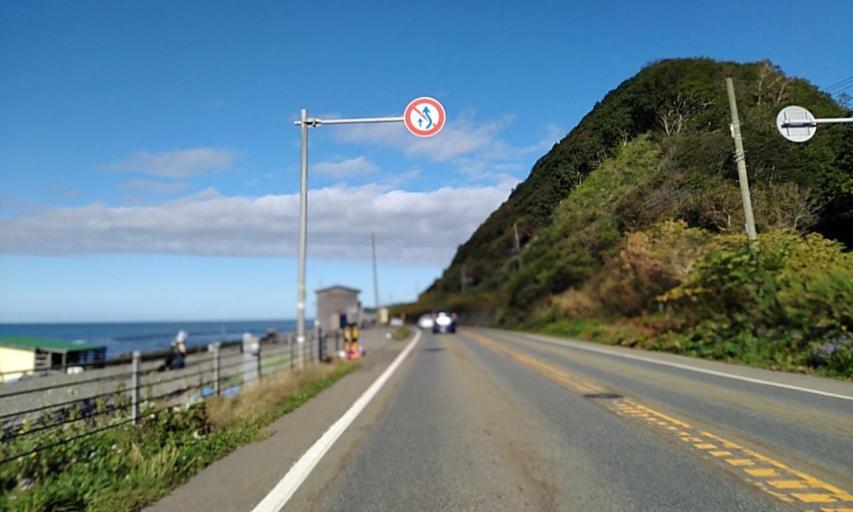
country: JP
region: Hokkaido
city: Shizunai-furukawacho
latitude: 42.2591
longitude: 142.5264
